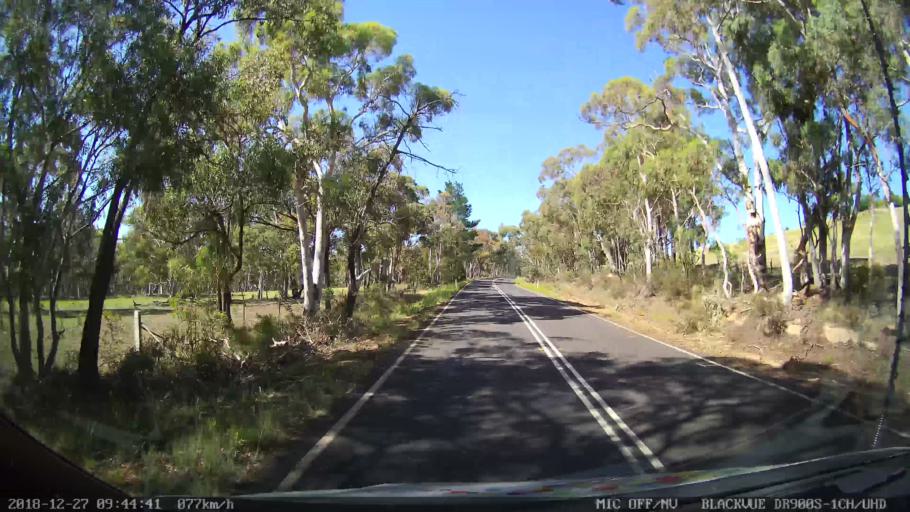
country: AU
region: New South Wales
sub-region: Lithgow
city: Portland
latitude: -33.3183
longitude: 149.9914
